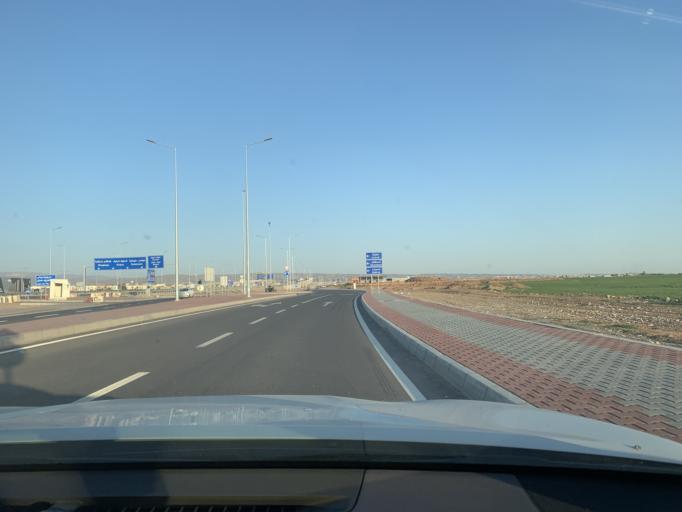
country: IQ
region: Arbil
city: Erbil
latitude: 36.2867
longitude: 44.0396
